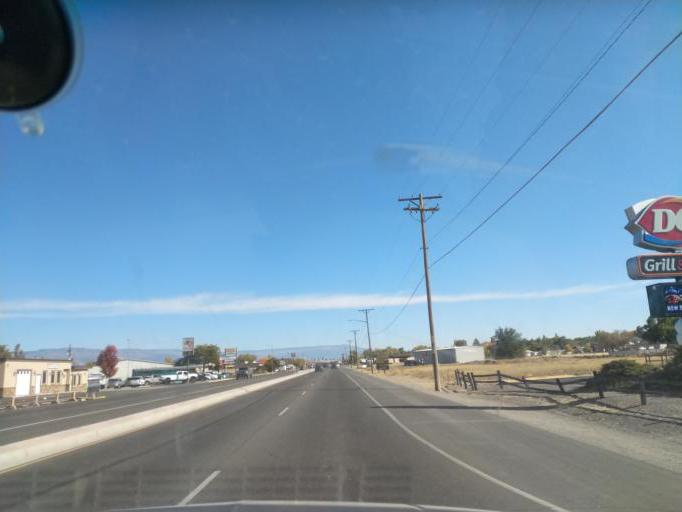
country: US
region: Colorado
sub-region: Mesa County
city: Orchard Mesa
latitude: 39.0446
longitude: -108.5569
